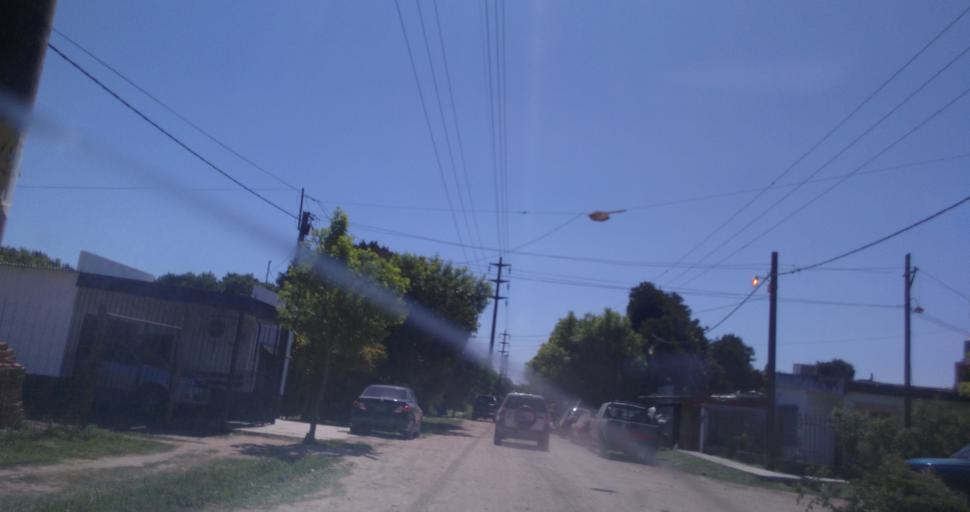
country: AR
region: Chaco
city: Resistencia
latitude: -27.4217
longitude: -58.9787
